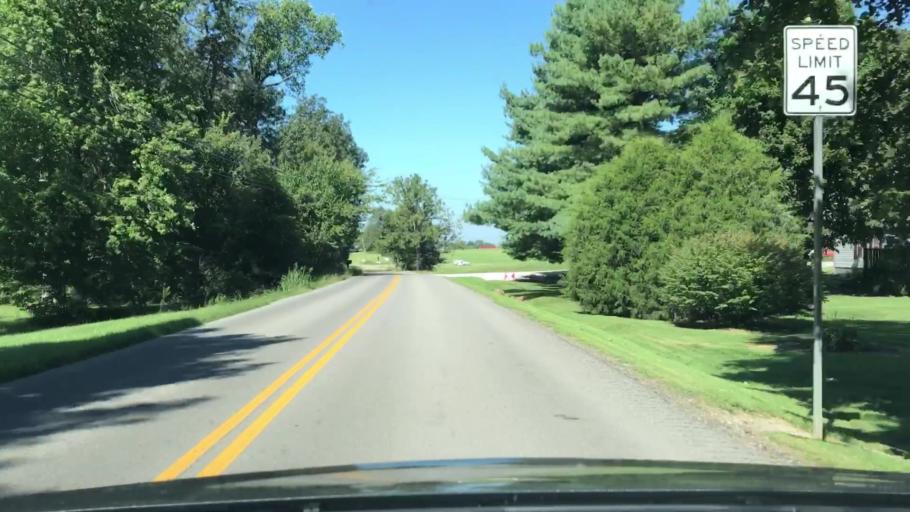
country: US
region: Kentucky
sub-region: Hardin County
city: Elizabethtown
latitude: 37.6016
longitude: -85.8848
